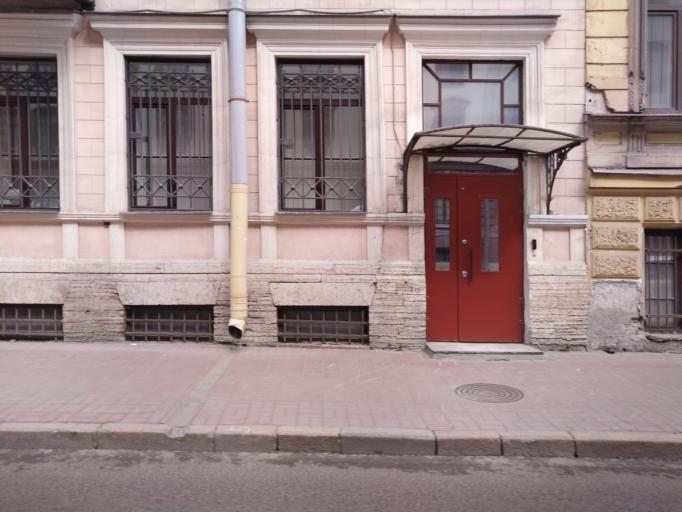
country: RU
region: St.-Petersburg
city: Centralniy
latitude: 59.9491
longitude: 30.3516
